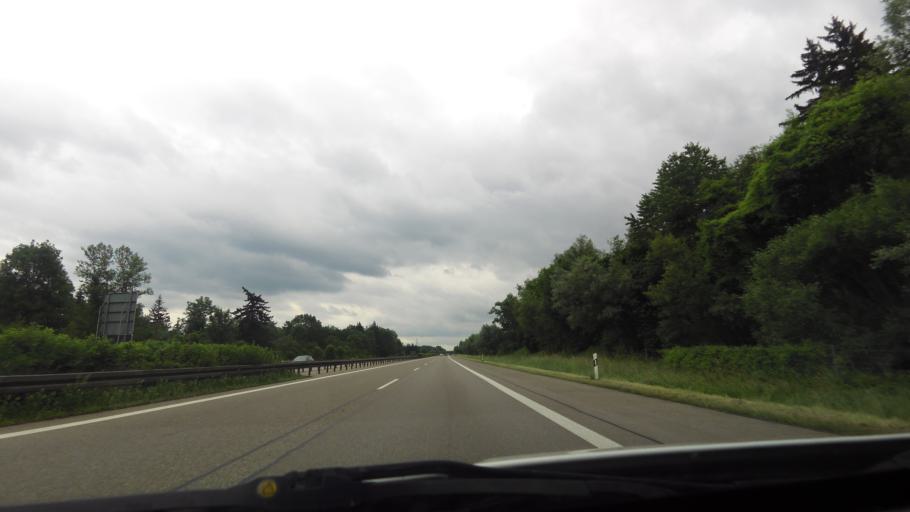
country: DE
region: Baden-Wuerttemberg
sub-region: Tuebingen Region
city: Kirchdorf
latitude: 48.0796
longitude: 10.1376
